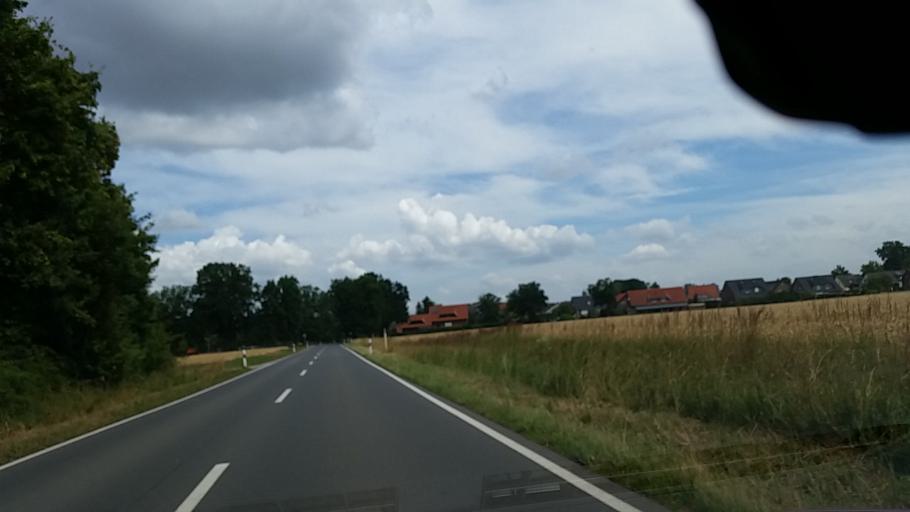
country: DE
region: Lower Saxony
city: Tiddische
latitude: 52.4962
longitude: 10.8005
